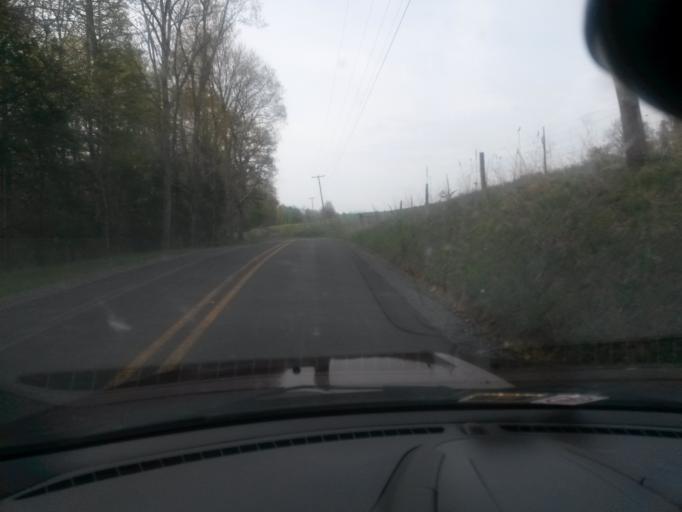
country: US
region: West Virginia
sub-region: Pocahontas County
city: Marlinton
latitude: 38.0999
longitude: -80.2264
